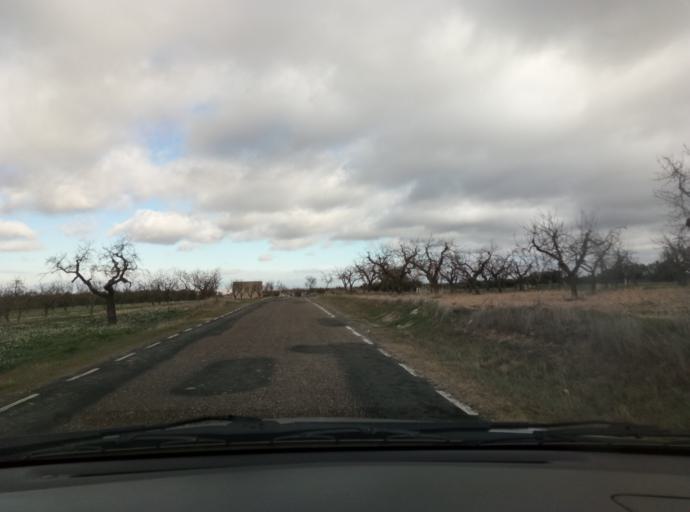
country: ES
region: Catalonia
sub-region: Provincia de Lleida
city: Nalec
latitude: 41.5779
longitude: 1.0758
